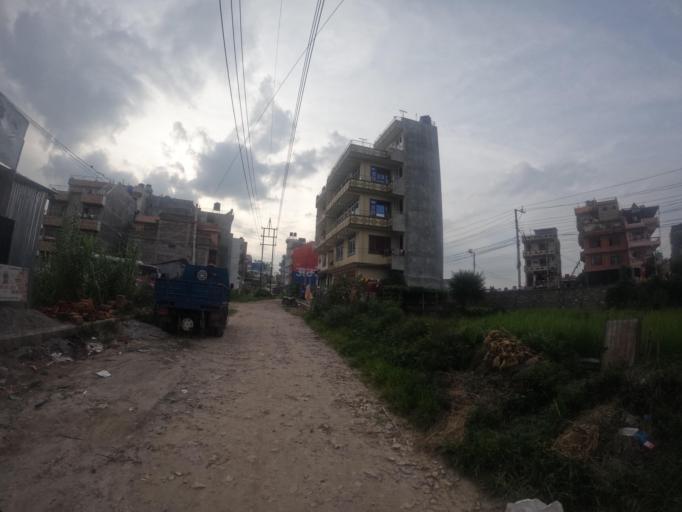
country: NP
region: Central Region
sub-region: Bagmati Zone
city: Bhaktapur
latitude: 27.6804
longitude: 85.3957
